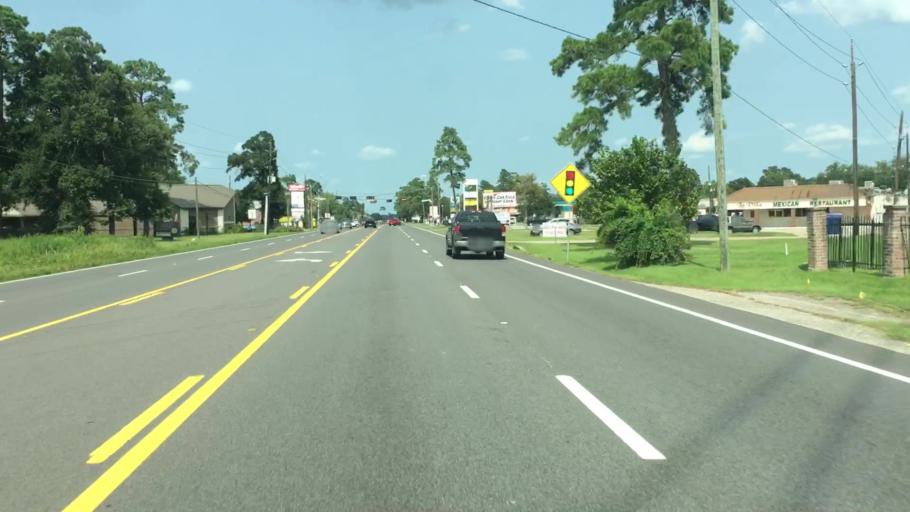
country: US
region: Texas
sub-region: Harris County
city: Atascocita
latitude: 30.0020
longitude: -95.1553
